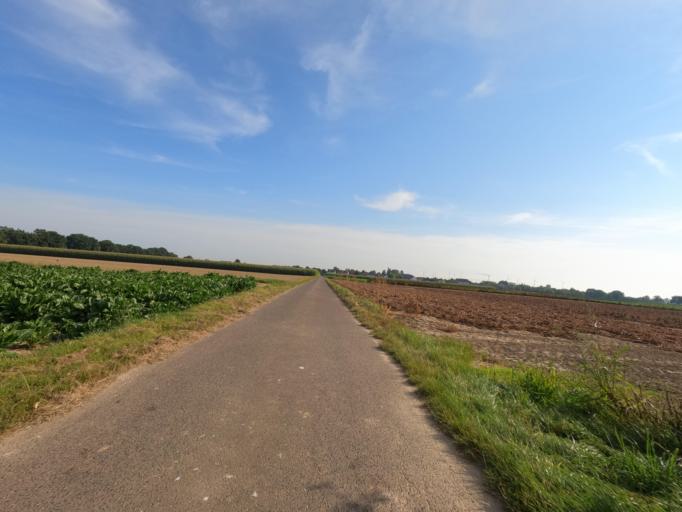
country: DE
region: North Rhine-Westphalia
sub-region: Regierungsbezirk Koln
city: Linnich
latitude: 51.0022
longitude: 6.2263
